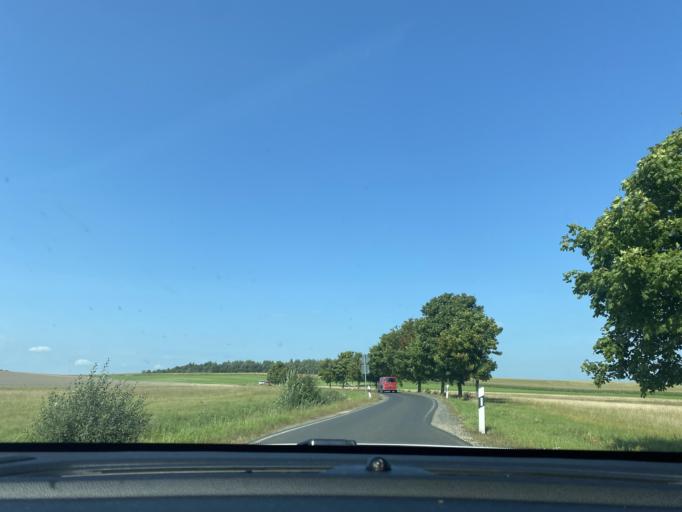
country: DE
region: Saxony
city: Quitzdorf
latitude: 51.2232
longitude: 14.7758
